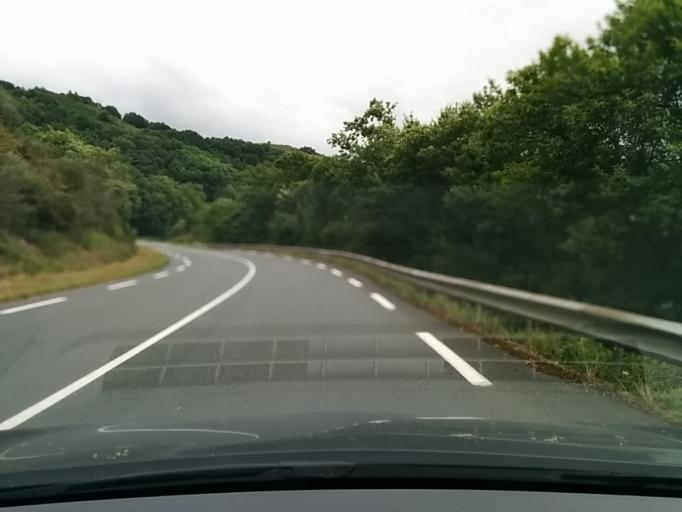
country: FR
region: Aquitaine
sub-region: Departement des Pyrenees-Atlantiques
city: Itxassou
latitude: 43.3044
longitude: -1.3568
